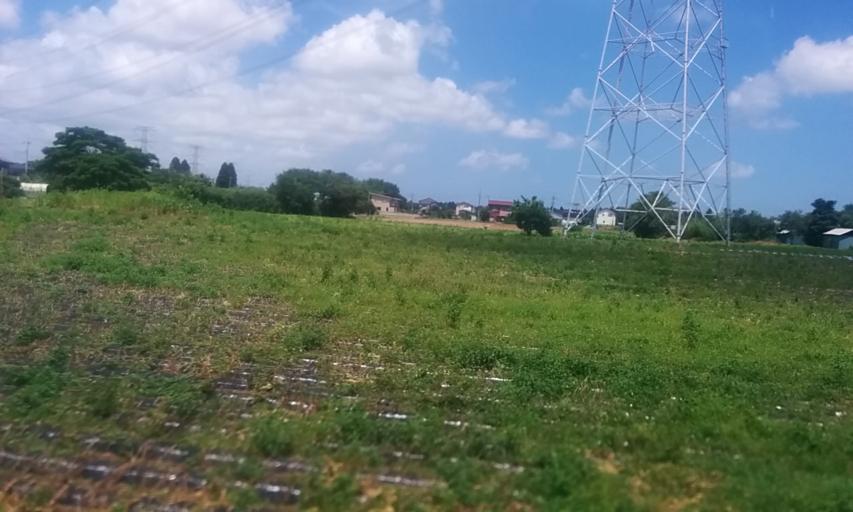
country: JP
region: Chiba
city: Oami
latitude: 35.5368
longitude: 140.2480
